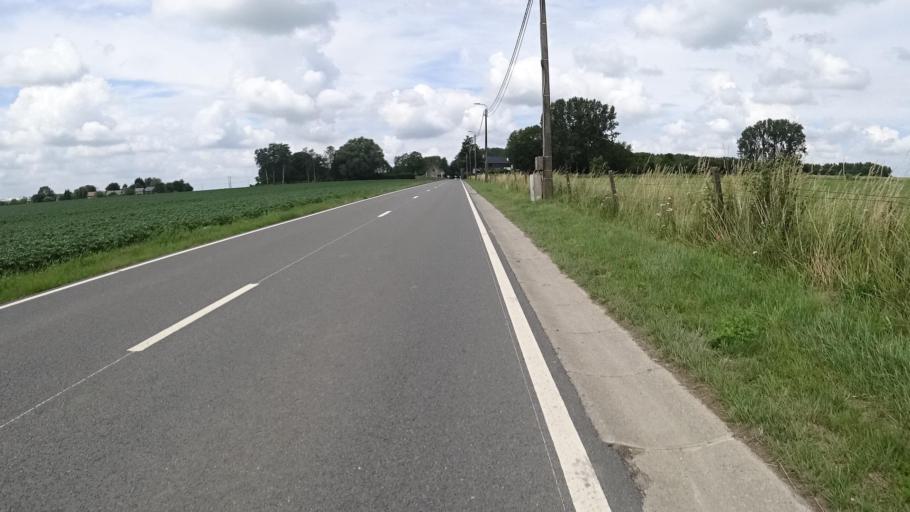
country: BE
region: Wallonia
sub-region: Province de Namur
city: Namur
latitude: 50.5391
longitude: 4.8419
